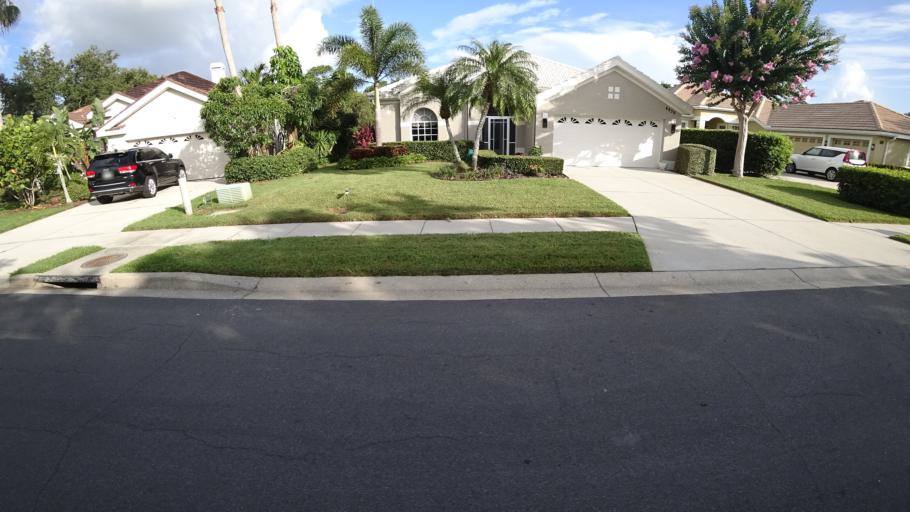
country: US
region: Florida
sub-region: Sarasota County
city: Desoto Lakes
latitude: 27.4229
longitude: -82.4870
